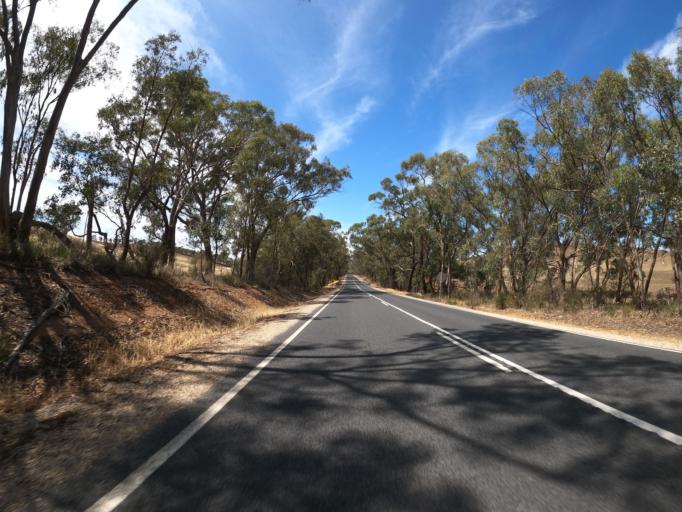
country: AU
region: Victoria
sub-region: Benalla
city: Benalla
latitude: -36.3789
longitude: 145.9762
